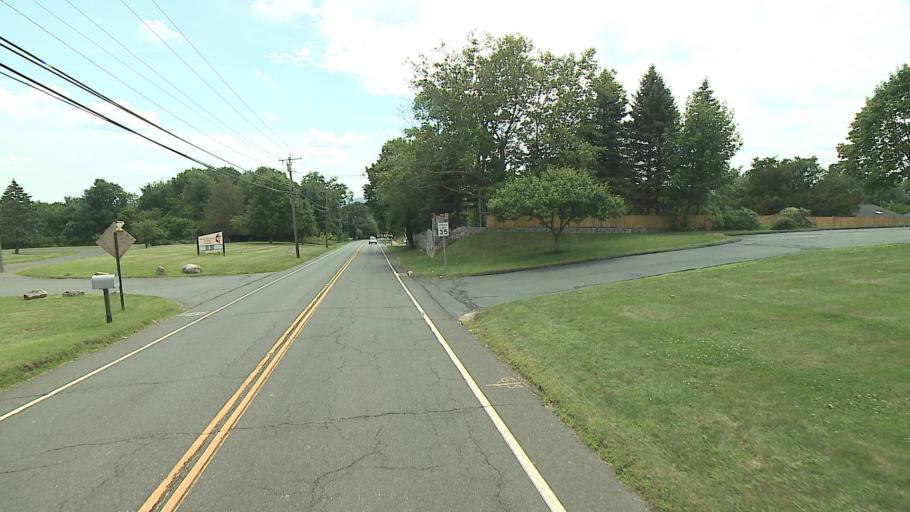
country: US
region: Connecticut
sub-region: Fairfield County
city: Danbury
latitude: 41.4099
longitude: -73.4686
